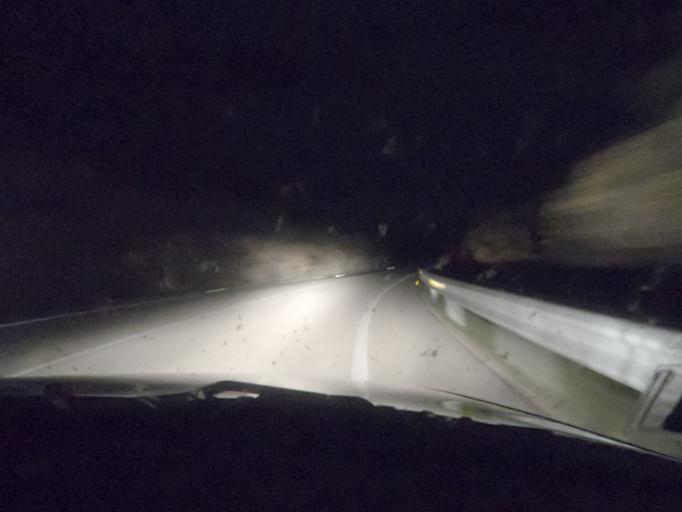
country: ES
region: Extremadura
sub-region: Provincia de Caceres
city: Acebo
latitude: 40.2293
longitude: -6.6807
